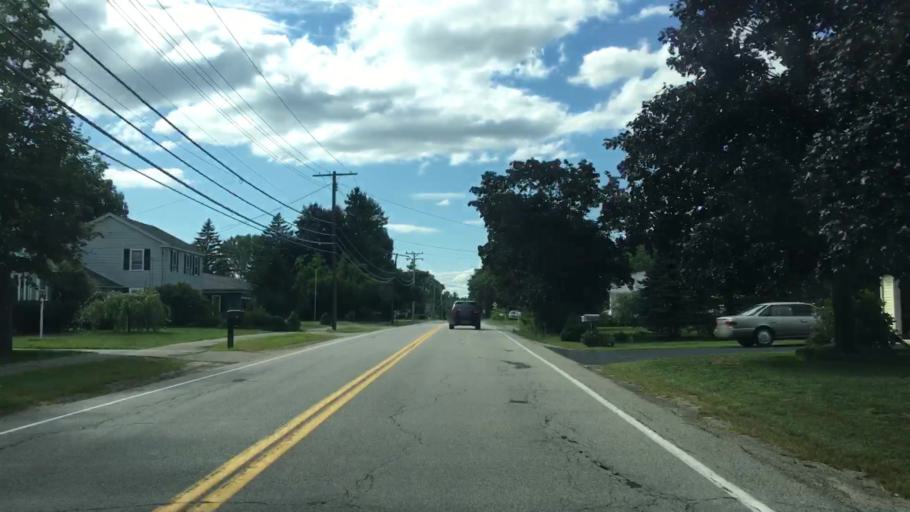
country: US
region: New Hampshire
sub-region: Strafford County
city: Somersworth
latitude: 43.2591
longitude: -70.8772
